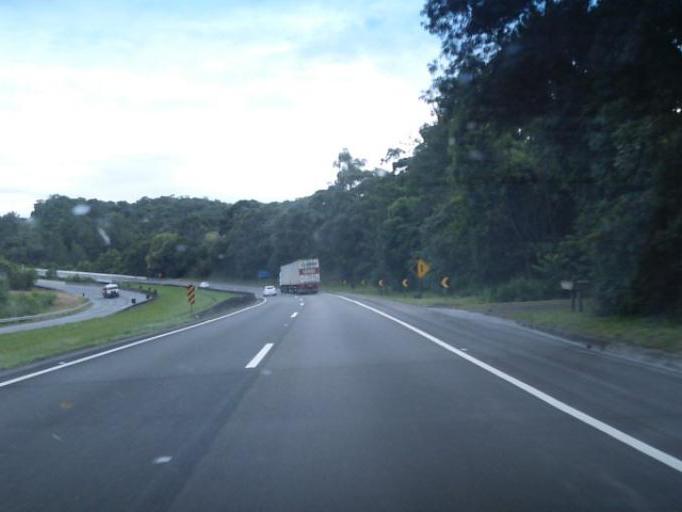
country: BR
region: Parana
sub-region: Campina Grande Do Sul
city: Campina Grande do Sul
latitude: -25.2008
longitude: -48.8959
